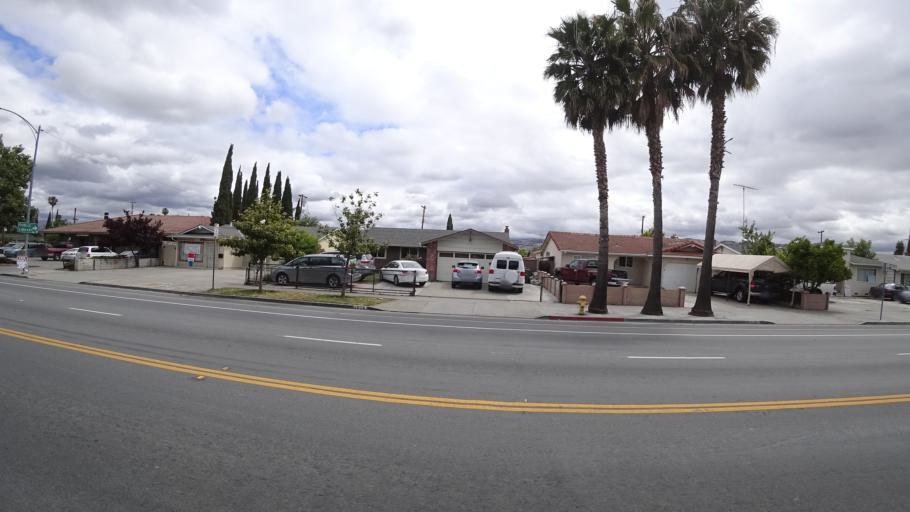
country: US
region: California
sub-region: Santa Clara County
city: Alum Rock
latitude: 37.3304
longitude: -121.8340
